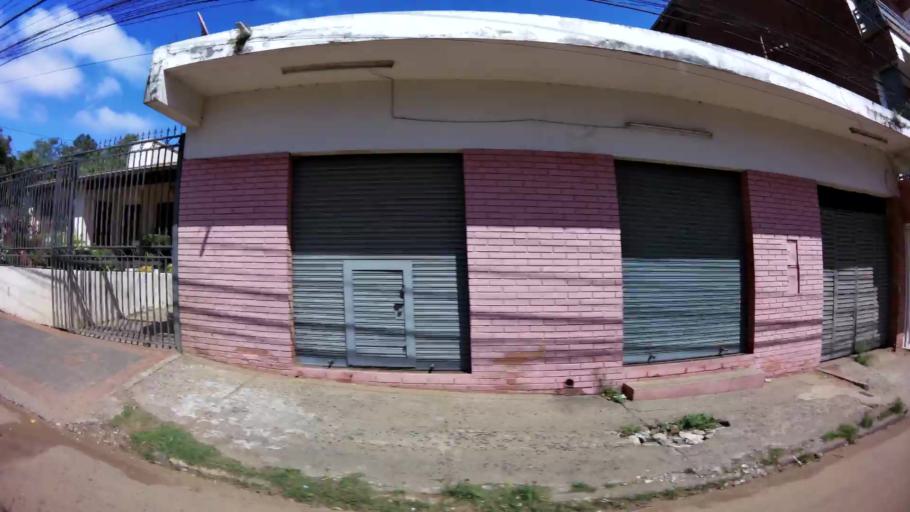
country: PY
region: Central
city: San Lorenzo
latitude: -25.2555
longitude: -57.4891
